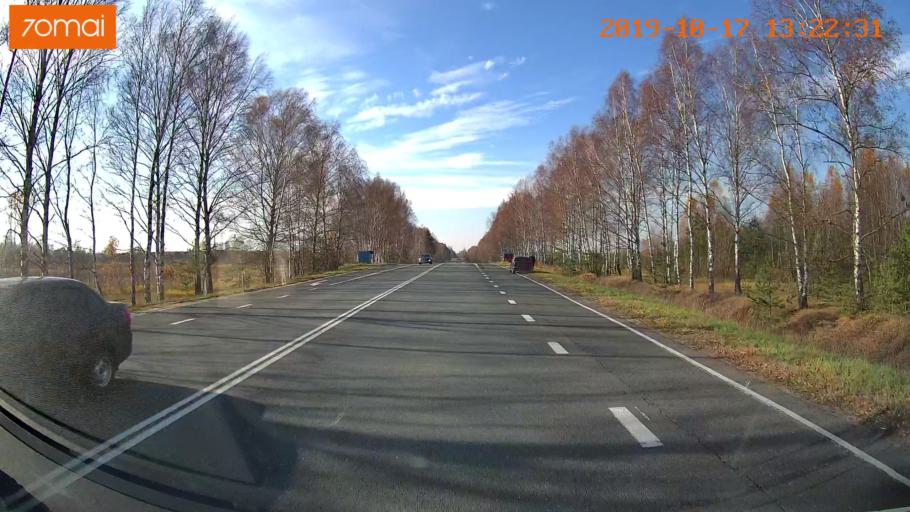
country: RU
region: Rjazan
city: Gus'-Zheleznyy
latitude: 55.0862
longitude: 41.0012
